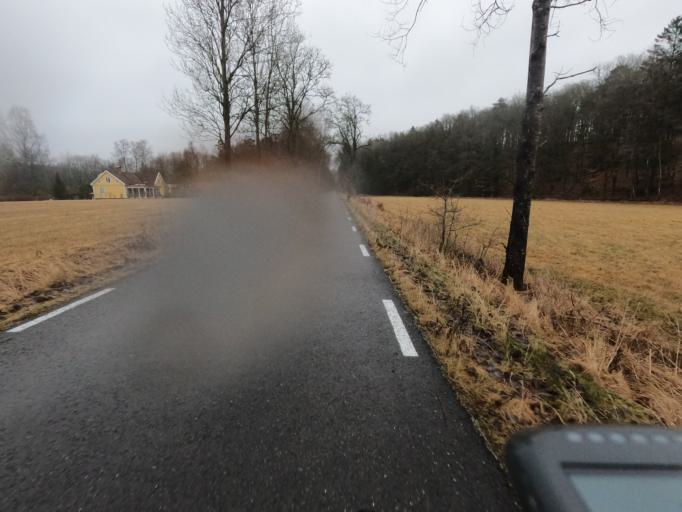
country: SE
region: Halland
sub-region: Halmstads Kommun
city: Aled
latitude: 56.7007
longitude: 13.0213
